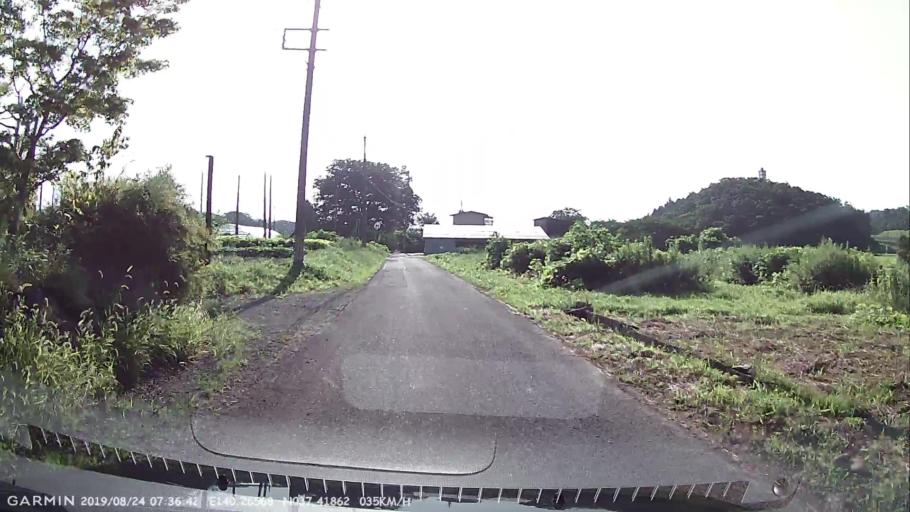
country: JP
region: Fukushima
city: Koriyama
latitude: 37.4186
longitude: 140.2658
